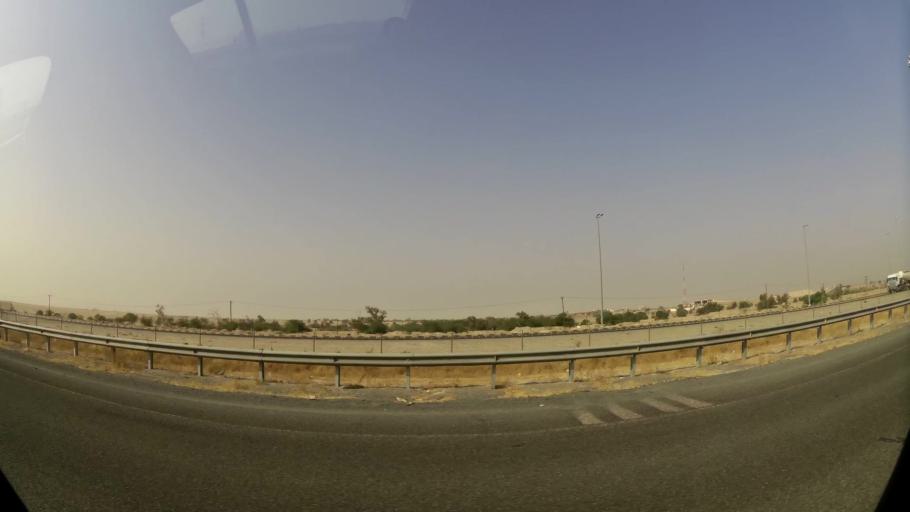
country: KW
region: Al Asimah
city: Ar Rabiyah
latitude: 29.2335
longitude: 47.8840
